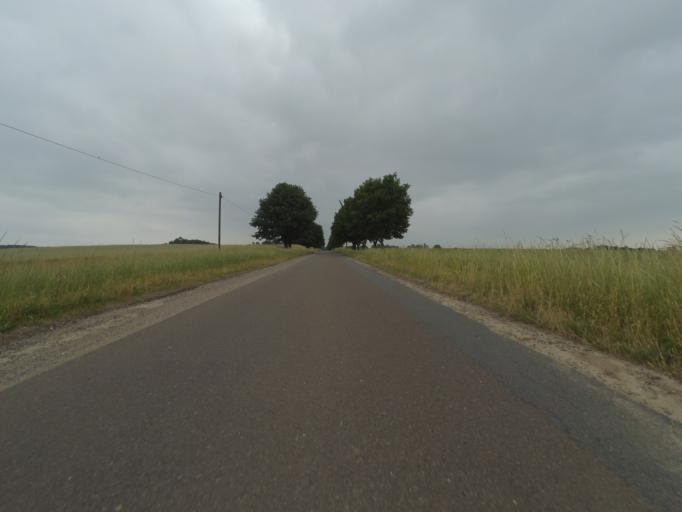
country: DE
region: Mecklenburg-Vorpommern
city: Spornitz
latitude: 53.3604
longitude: 11.7213
